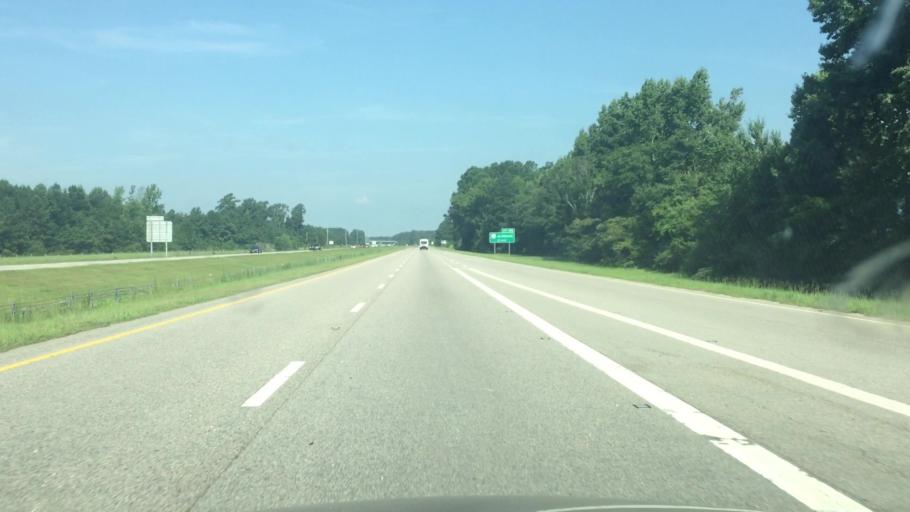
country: US
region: North Carolina
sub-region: Robeson County
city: Lumberton
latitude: 34.5817
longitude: -79.0515
